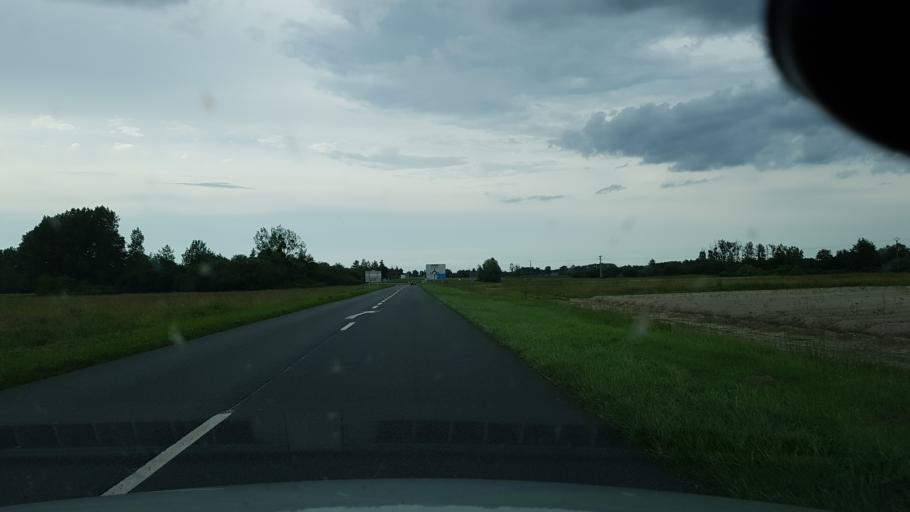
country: FR
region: Centre
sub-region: Departement du Loir-et-Cher
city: Chatillon-sur-Cher
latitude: 47.3181
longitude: 1.4984
